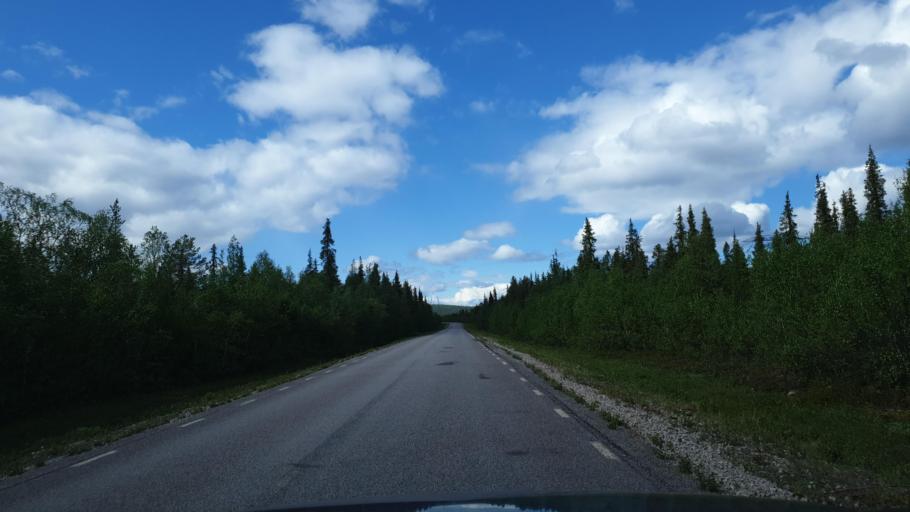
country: SE
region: Norrbotten
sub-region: Jokkmokks Kommun
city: Jokkmokk
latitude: 67.0944
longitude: 19.7528
